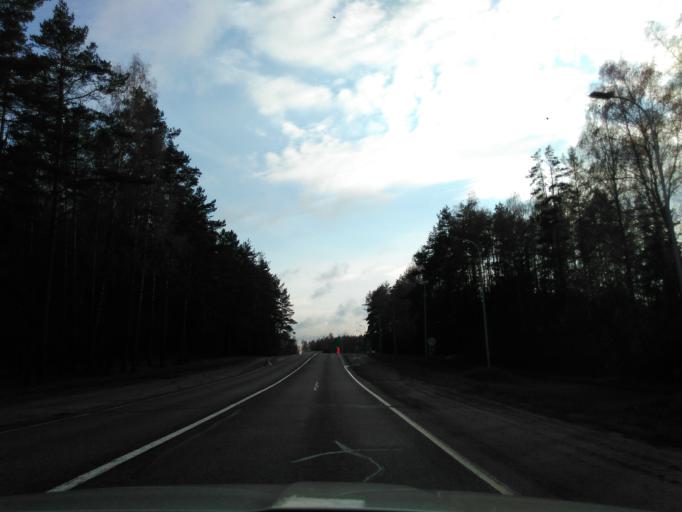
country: BY
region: Minsk
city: Lahoysk
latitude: 54.2472
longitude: 27.8474
